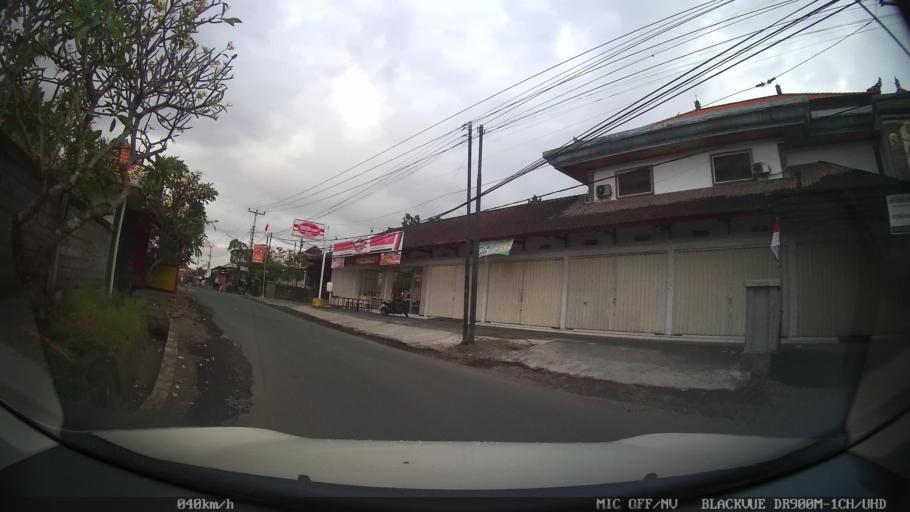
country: ID
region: Bali
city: Banjar Pasekan
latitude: -8.6386
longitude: 115.2751
